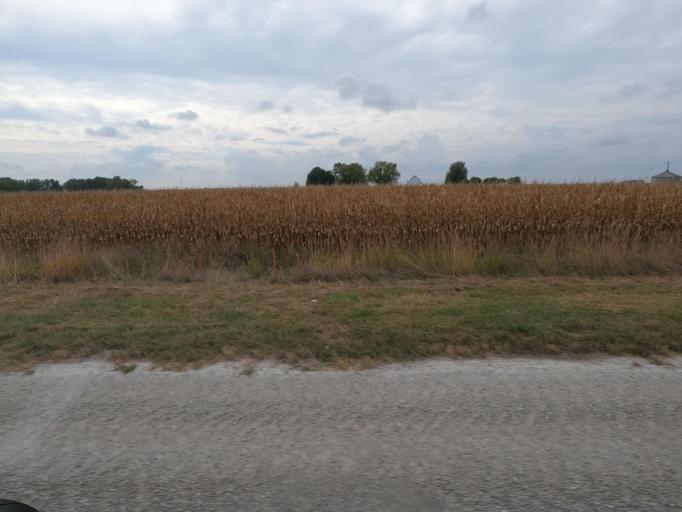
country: US
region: Iowa
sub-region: Jasper County
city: Monroe
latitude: 41.5034
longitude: -93.0812
